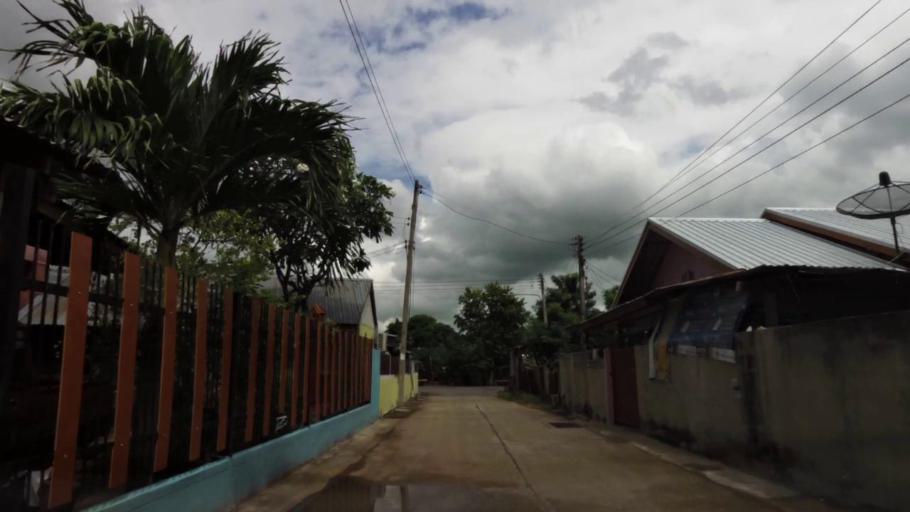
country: TH
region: Nakhon Sawan
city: Phai Sali
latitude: 15.6024
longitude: 100.6536
